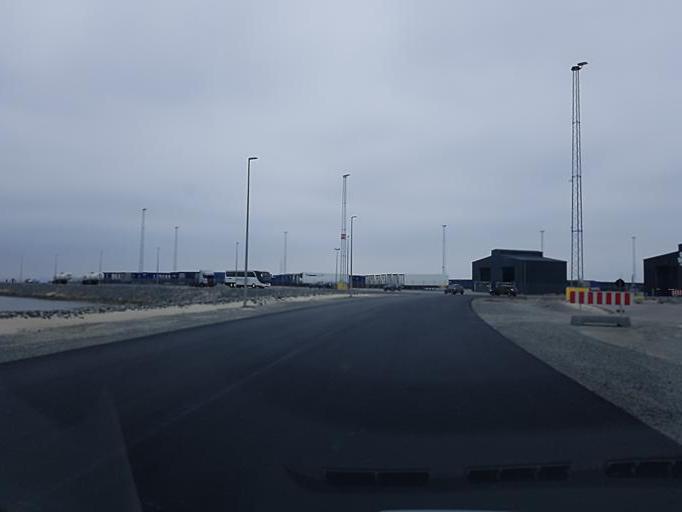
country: DK
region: South Denmark
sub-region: Esbjerg Kommune
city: Esbjerg
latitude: 55.4548
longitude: 8.4893
